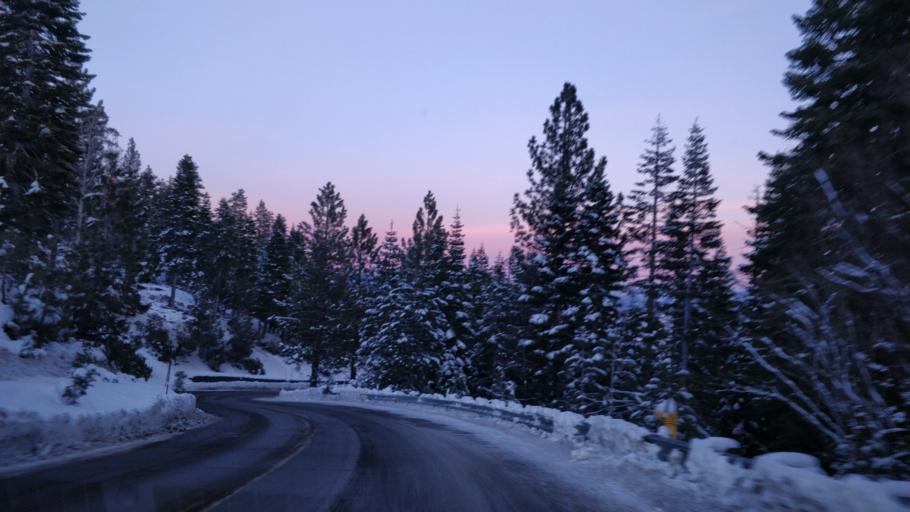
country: US
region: California
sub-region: Placer County
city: Sunnyside-Tahoe City
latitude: 39.1415
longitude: -120.1658
